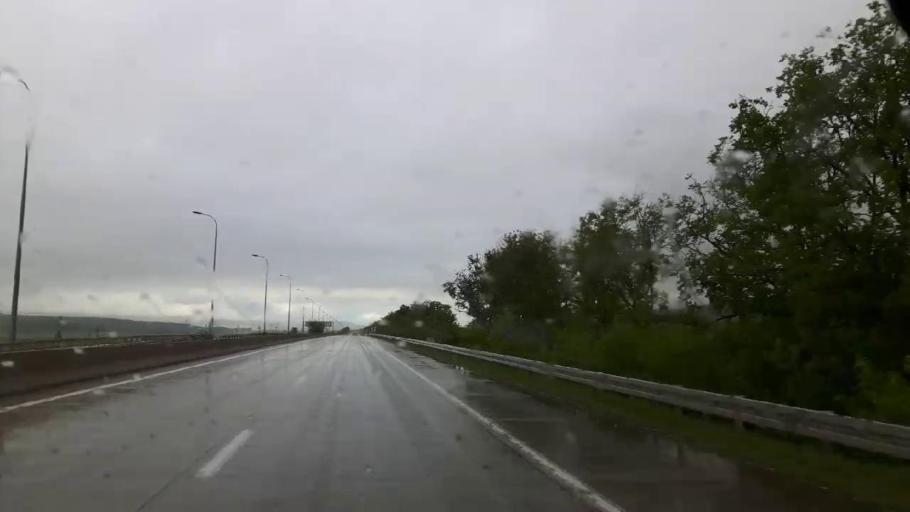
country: GE
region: Shida Kartli
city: Kaspi
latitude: 42.0210
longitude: 44.2975
